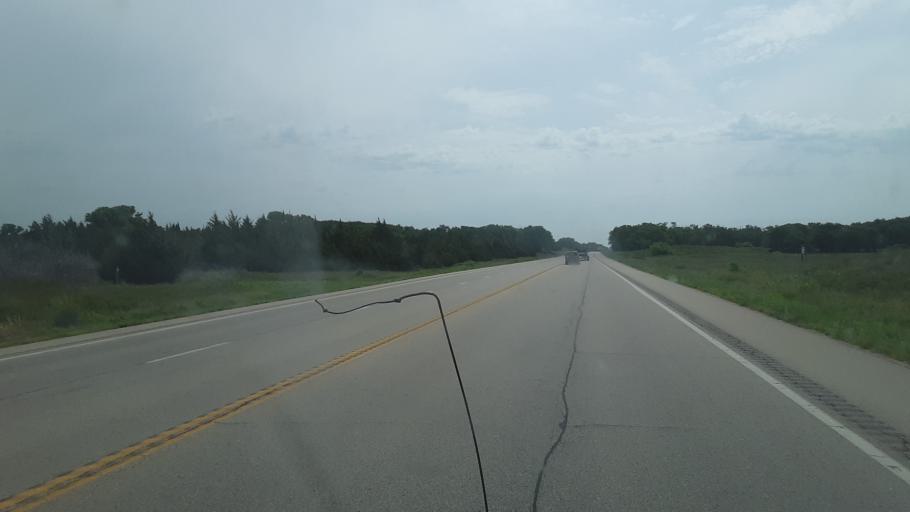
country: US
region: Kansas
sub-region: Rice County
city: Sterling
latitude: 37.9850
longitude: -98.2764
